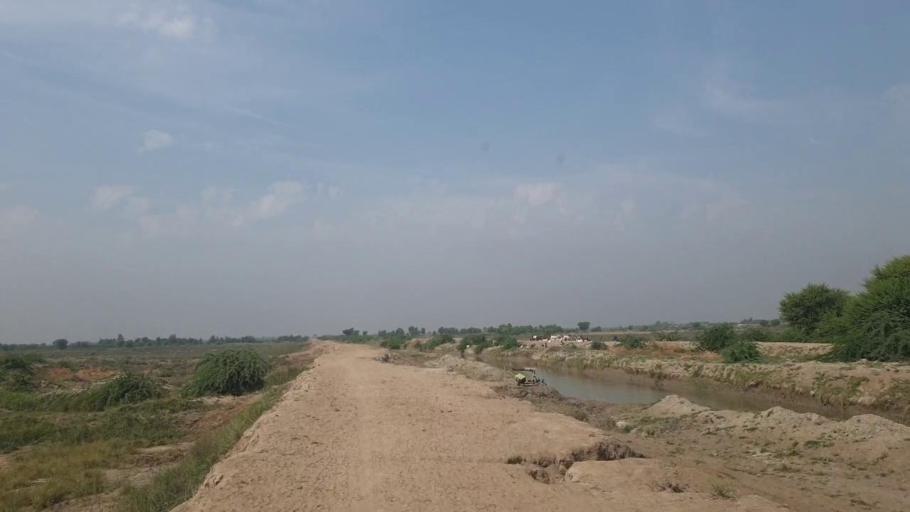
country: PK
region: Sindh
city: Rajo Khanani
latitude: 24.9578
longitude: 69.0269
